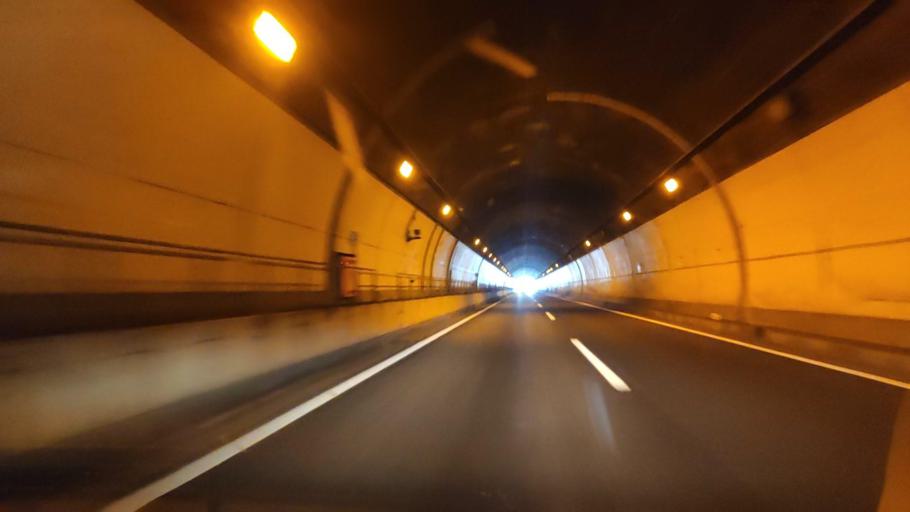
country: JP
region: Akita
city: Hanawa
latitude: 40.0161
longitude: 140.9860
